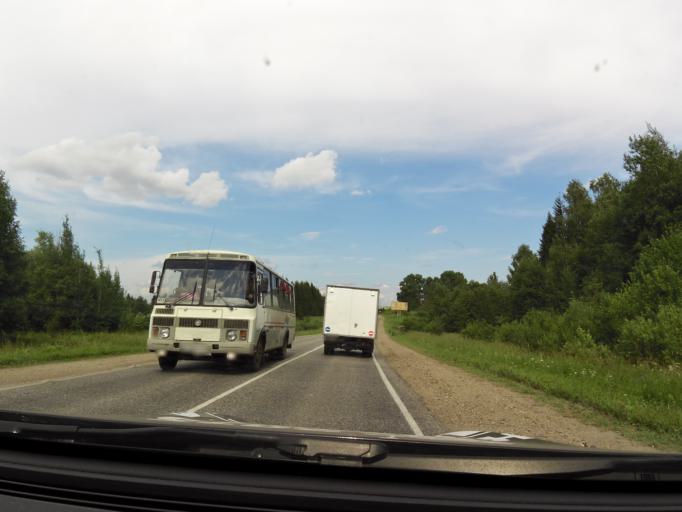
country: RU
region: Kirov
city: Stulovo
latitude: 58.7072
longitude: 50.0991
